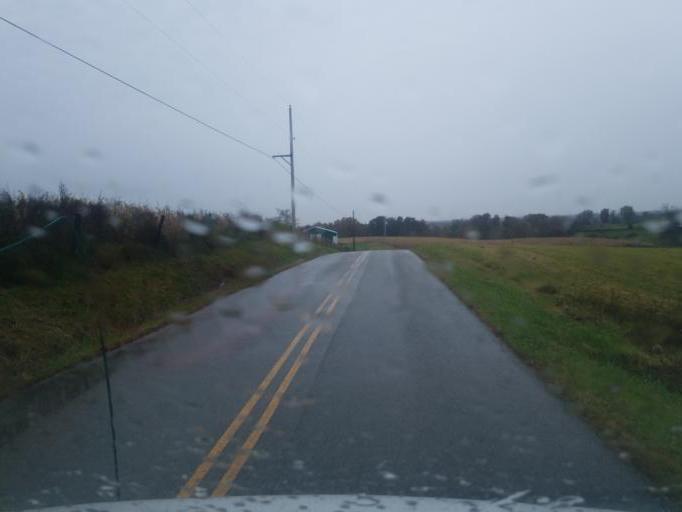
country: US
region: Ohio
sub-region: Washington County
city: Beverly
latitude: 39.4574
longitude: -81.6257
